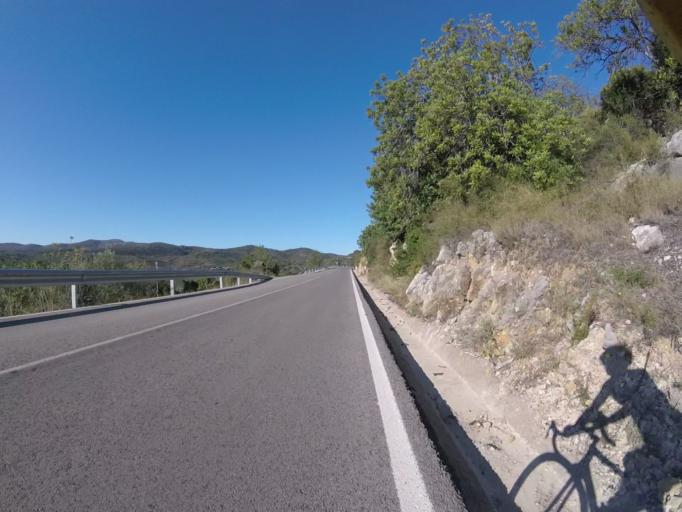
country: ES
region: Valencia
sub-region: Provincia de Castello
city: Cervera del Maestre
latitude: 40.4566
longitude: 0.2682
